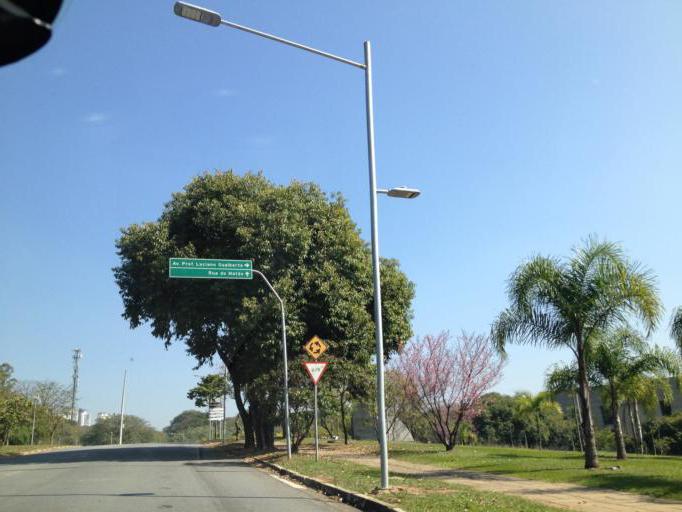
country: BR
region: Sao Paulo
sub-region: Osasco
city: Osasco
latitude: -23.5628
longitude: -46.7201
